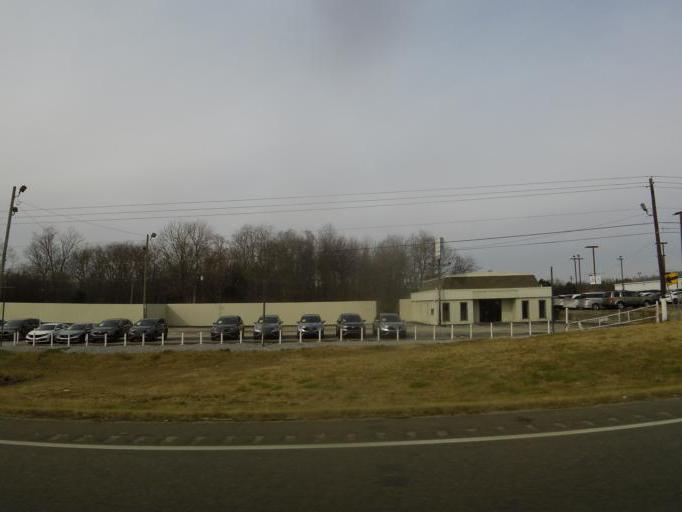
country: US
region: Alabama
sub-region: Montgomery County
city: Montgomery
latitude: 32.3412
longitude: -86.2258
